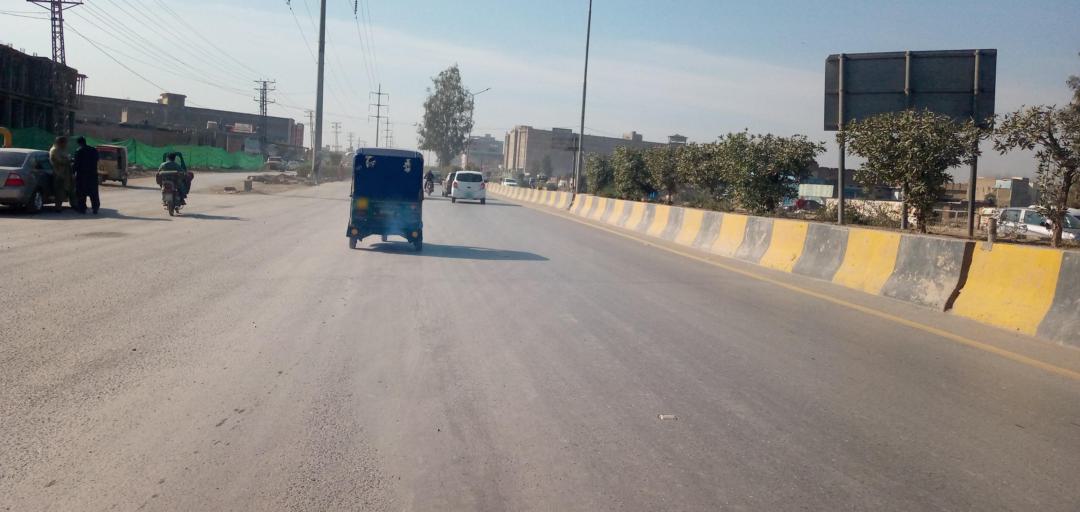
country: PK
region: Khyber Pakhtunkhwa
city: Peshawar
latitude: 33.9687
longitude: 71.5377
